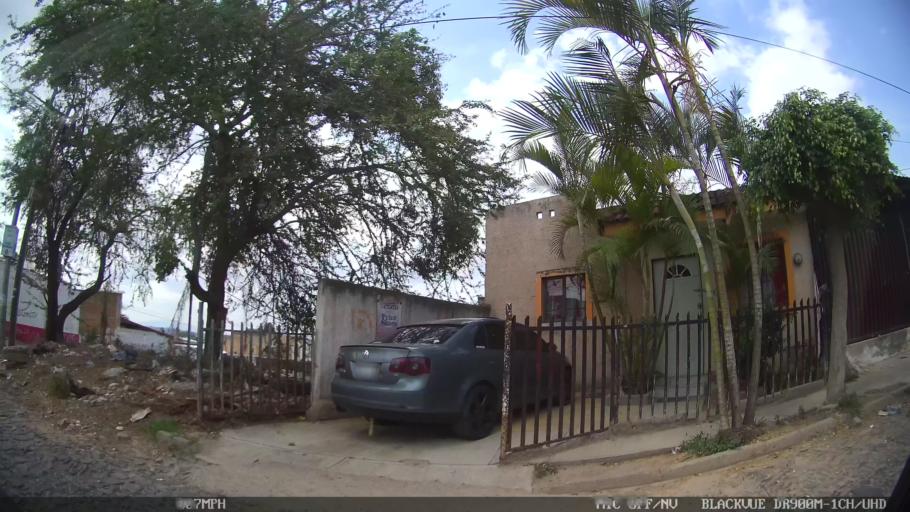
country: MX
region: Jalisco
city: Tonala
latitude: 20.6297
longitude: -103.2305
